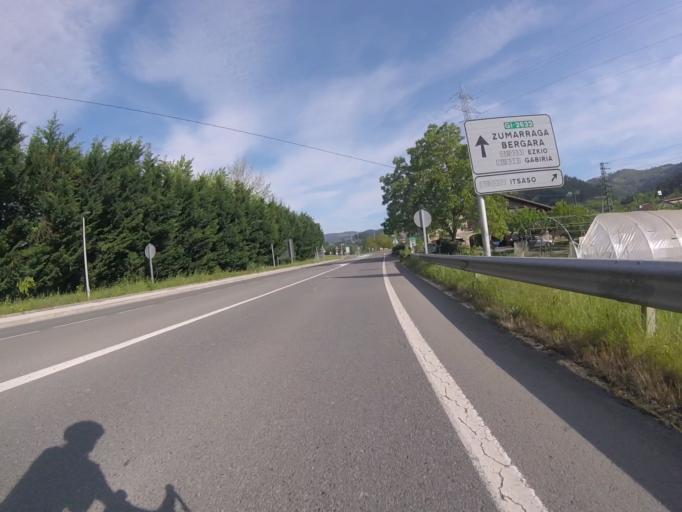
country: ES
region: Basque Country
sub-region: Provincia de Guipuzcoa
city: Ormaiztegui
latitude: 43.0517
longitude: -2.2623
